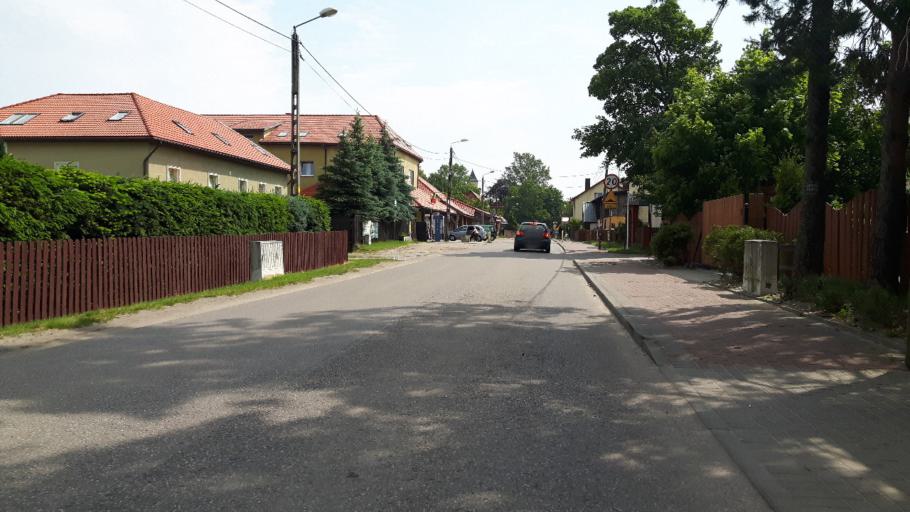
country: PL
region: Pomeranian Voivodeship
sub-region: Powiat leborski
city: Leba
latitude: 54.7526
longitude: 17.5844
